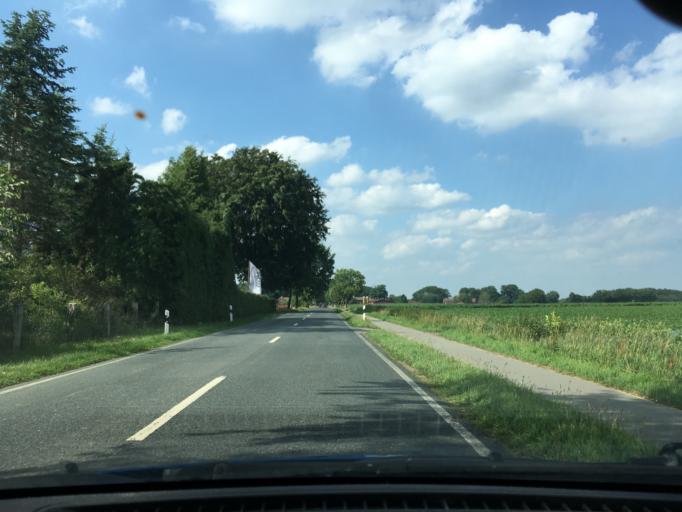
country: DE
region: Lower Saxony
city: Bendestorf
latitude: 53.3584
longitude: 9.9416
